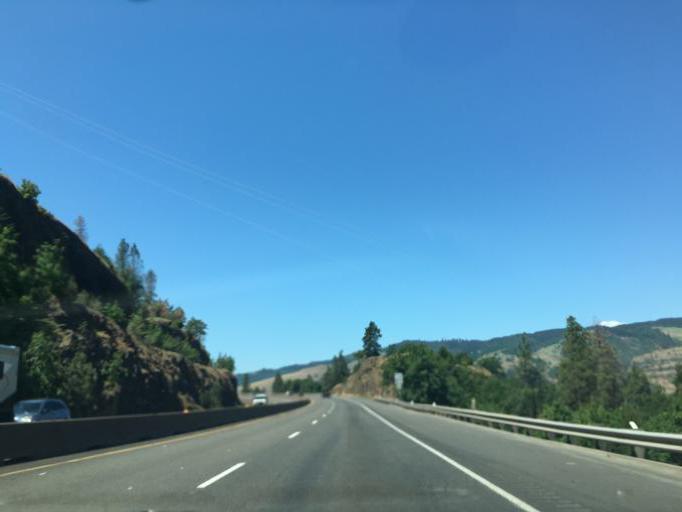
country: US
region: Oregon
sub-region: Wasco County
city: Chenoweth
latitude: 45.6961
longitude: -121.3498
